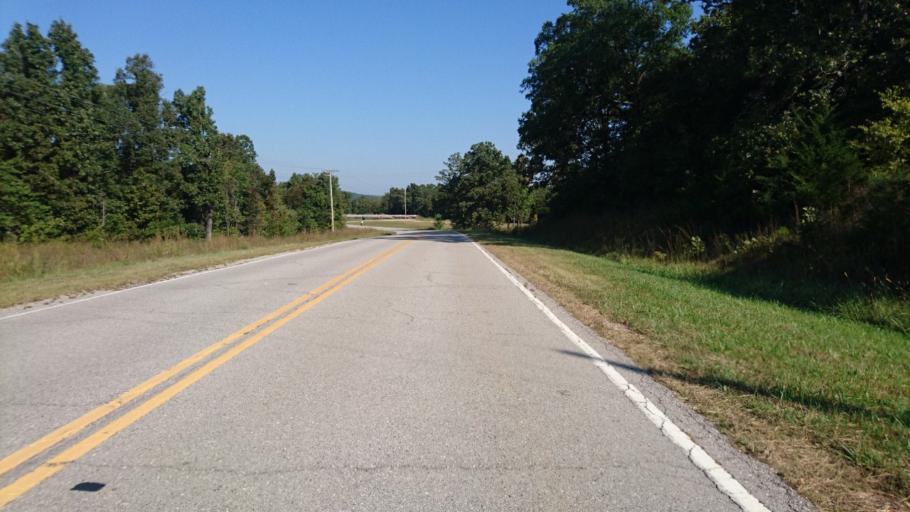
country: US
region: Missouri
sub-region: Pulaski County
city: Richland
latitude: 37.7567
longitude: -92.3743
